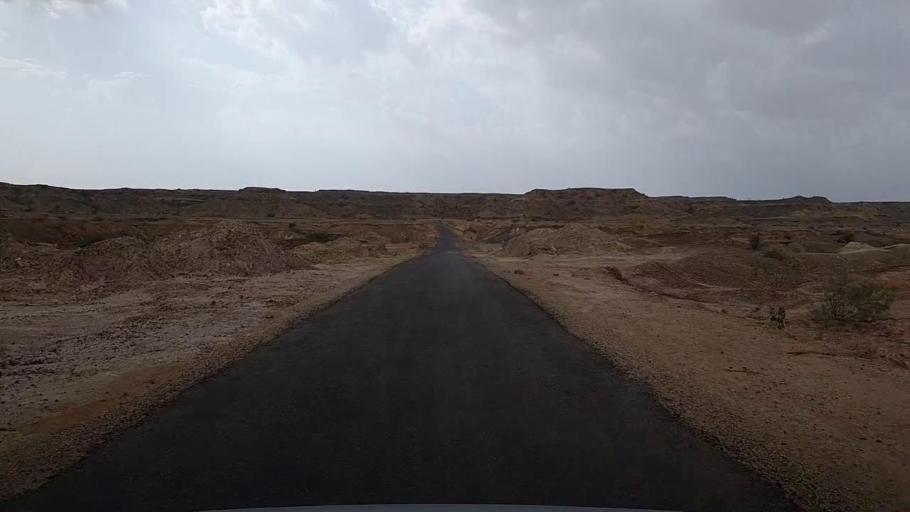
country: PK
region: Sindh
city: Jamshoro
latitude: 25.4198
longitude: 67.6936
